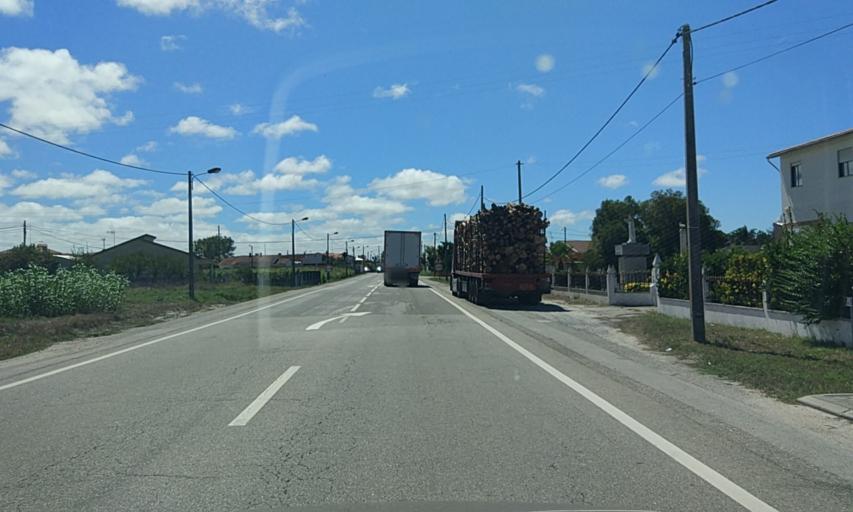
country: PT
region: Coimbra
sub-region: Mira
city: Mira
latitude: 40.4711
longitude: -8.6976
